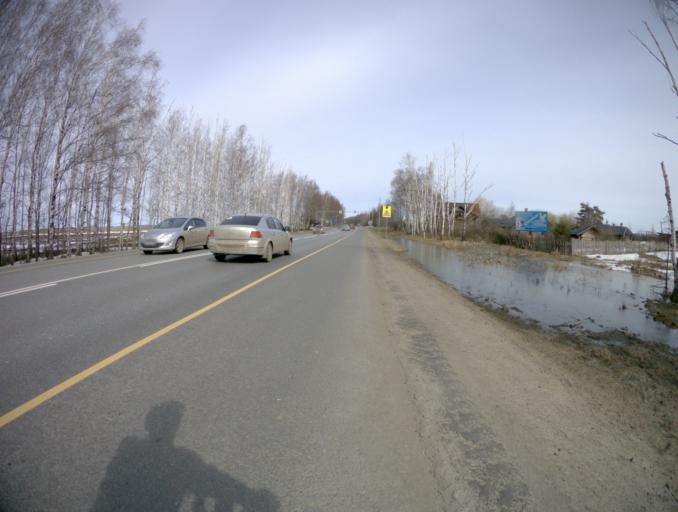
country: RU
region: Vladimir
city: Bogolyubovo
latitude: 56.2564
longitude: 40.4618
